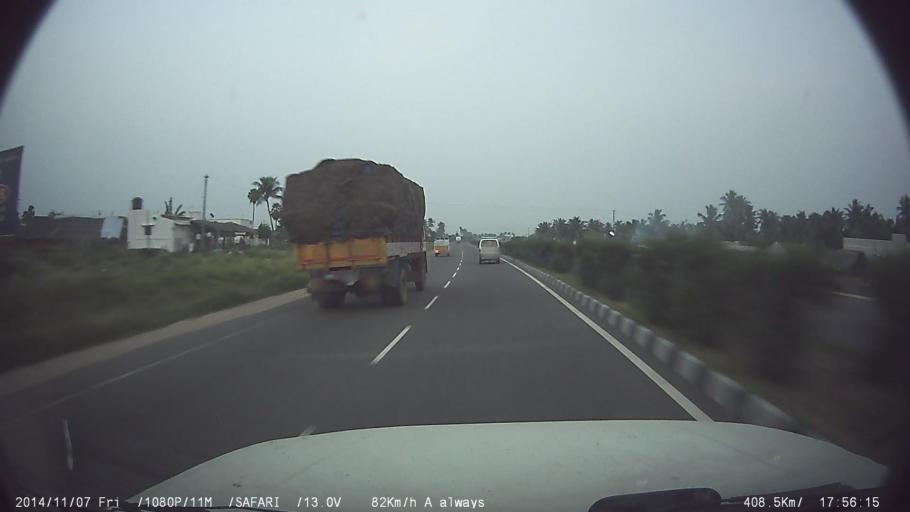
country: IN
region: Tamil Nadu
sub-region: Erode
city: Perundurai
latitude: 11.3229
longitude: 77.6255
